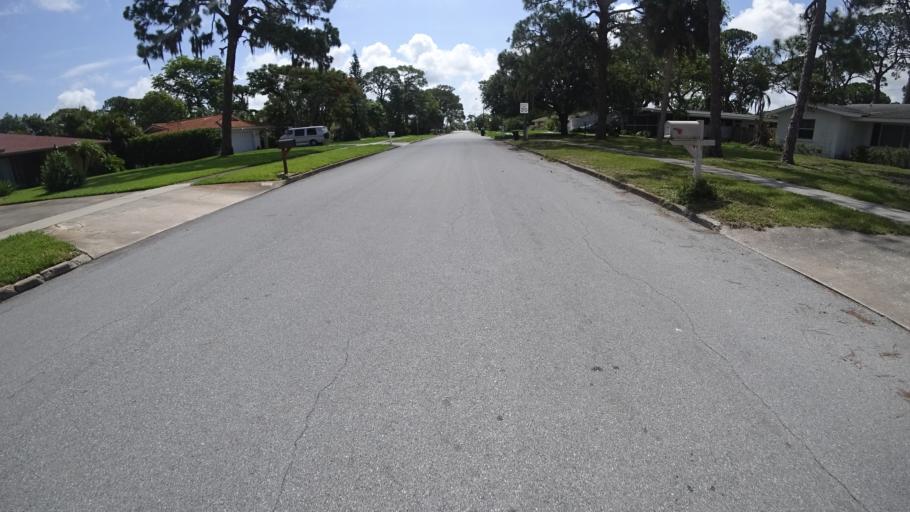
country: US
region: Florida
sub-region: Manatee County
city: Whitfield
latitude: 27.3977
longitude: -82.5661
